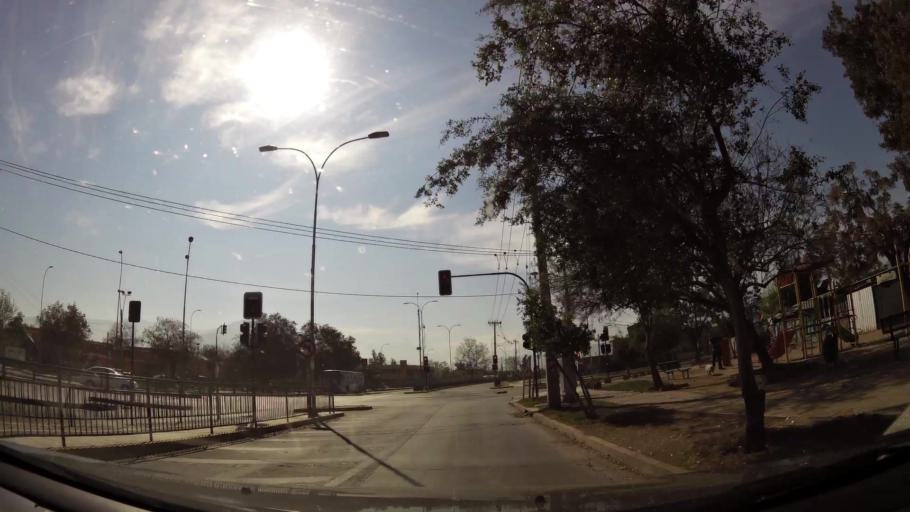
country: CL
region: Santiago Metropolitan
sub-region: Provincia de Santiago
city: Santiago
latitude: -33.3956
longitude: -70.6536
